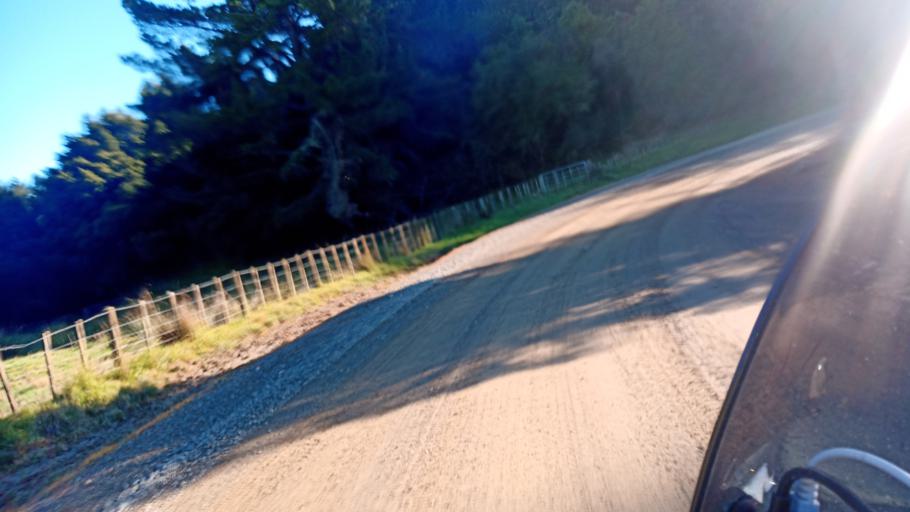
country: NZ
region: Hawke's Bay
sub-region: Wairoa District
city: Wairoa
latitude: -38.8113
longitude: 177.2879
